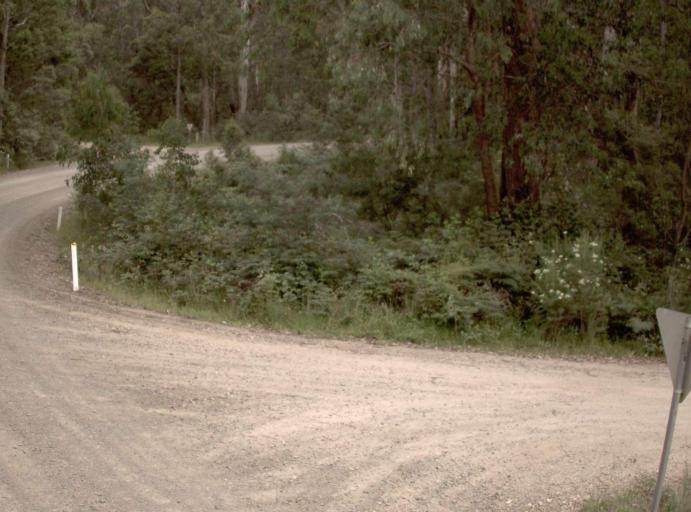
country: AU
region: Victoria
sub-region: East Gippsland
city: Bairnsdale
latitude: -37.7028
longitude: 147.5870
